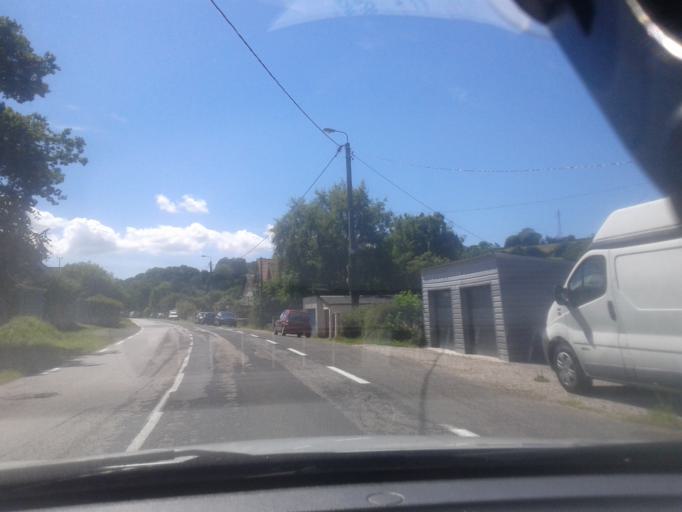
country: FR
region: Lower Normandy
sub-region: Departement de la Manche
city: Octeville
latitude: 49.6155
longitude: -1.6419
